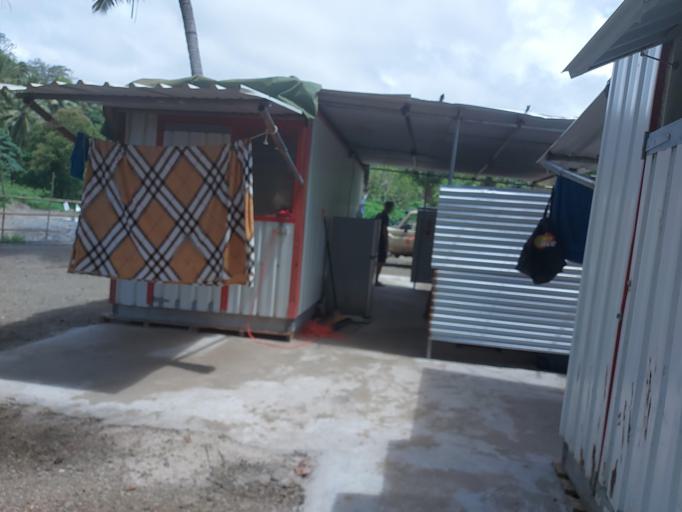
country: VU
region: Malampa
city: Lakatoro
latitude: -16.3114
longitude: 167.6959
